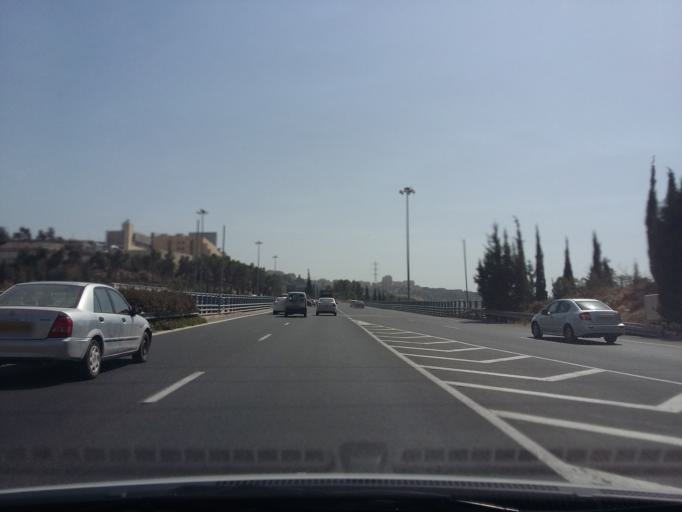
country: IL
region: Jerusalem
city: West Jerusalem
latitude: 31.8092
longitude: 35.2090
